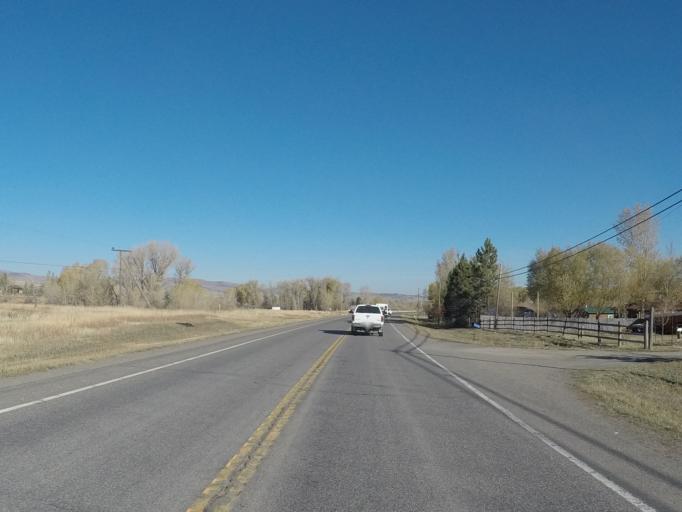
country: US
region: Montana
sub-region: Park County
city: Livingston
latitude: 45.6179
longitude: -110.5791
